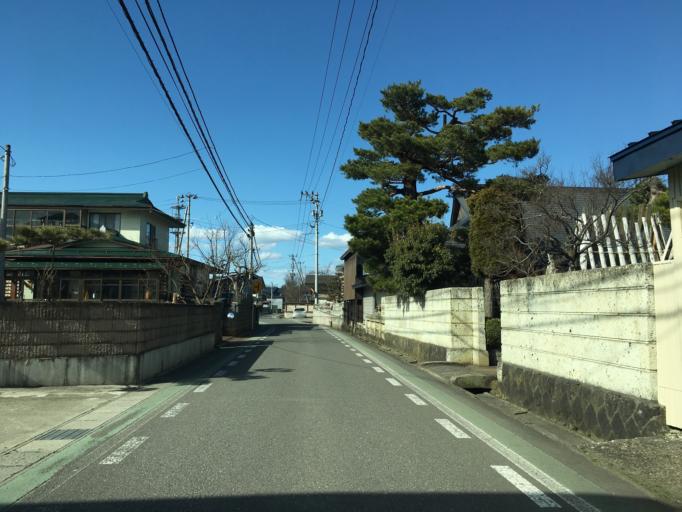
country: JP
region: Yamagata
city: Yonezawa
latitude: 37.9266
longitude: 140.1438
